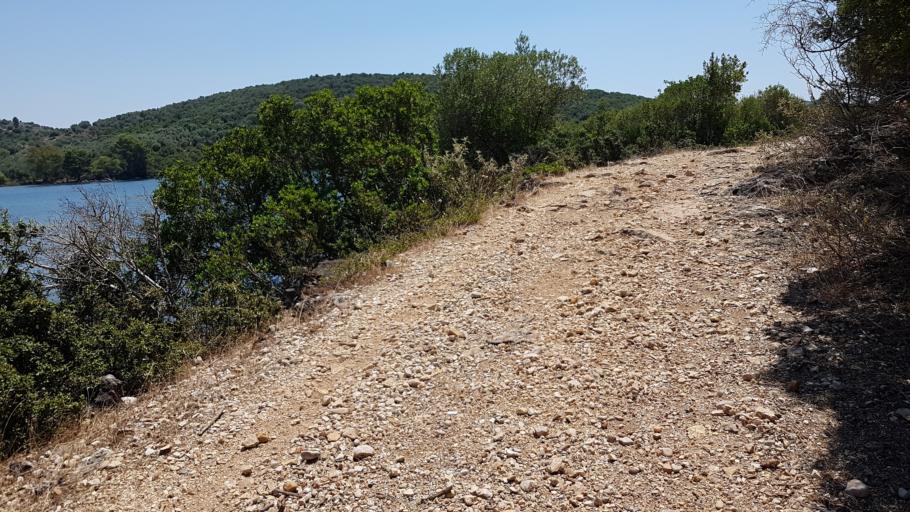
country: AL
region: Vlore
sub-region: Rrethi i Sarandes
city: Xarre
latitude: 39.7521
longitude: 19.9960
